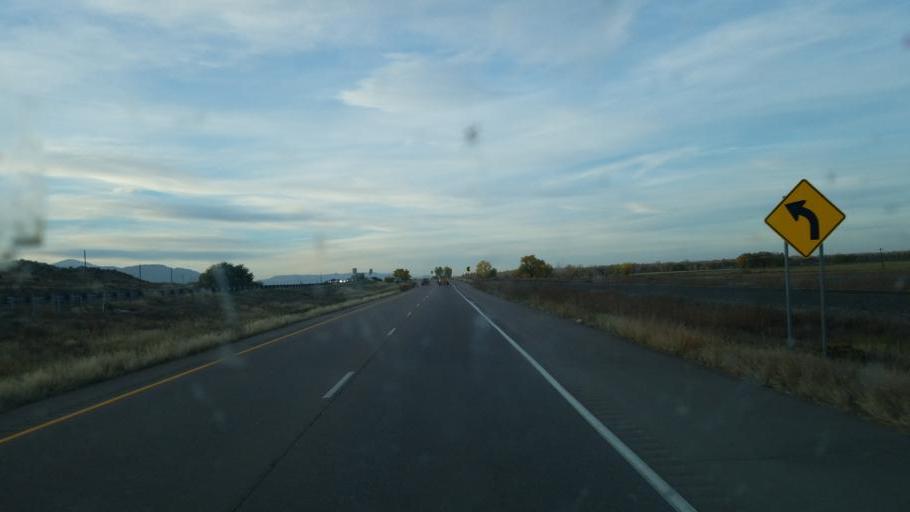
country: US
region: Colorado
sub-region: El Paso County
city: Fountain
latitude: 38.5695
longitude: -104.6552
